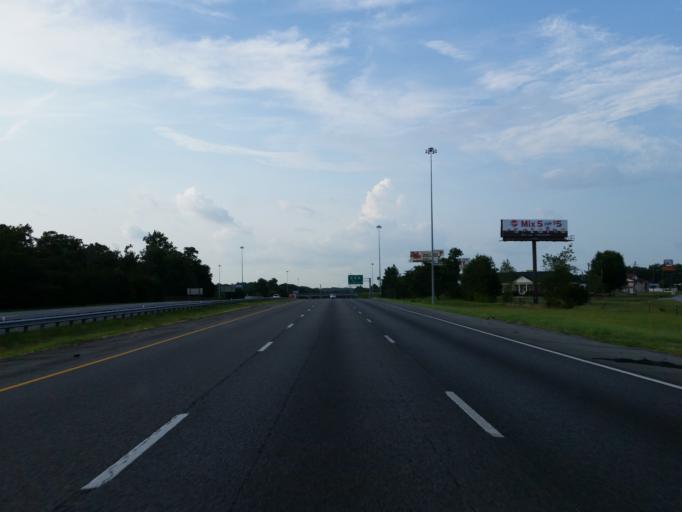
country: US
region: Georgia
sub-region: Houston County
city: Perry
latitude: 32.4413
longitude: -83.7553
